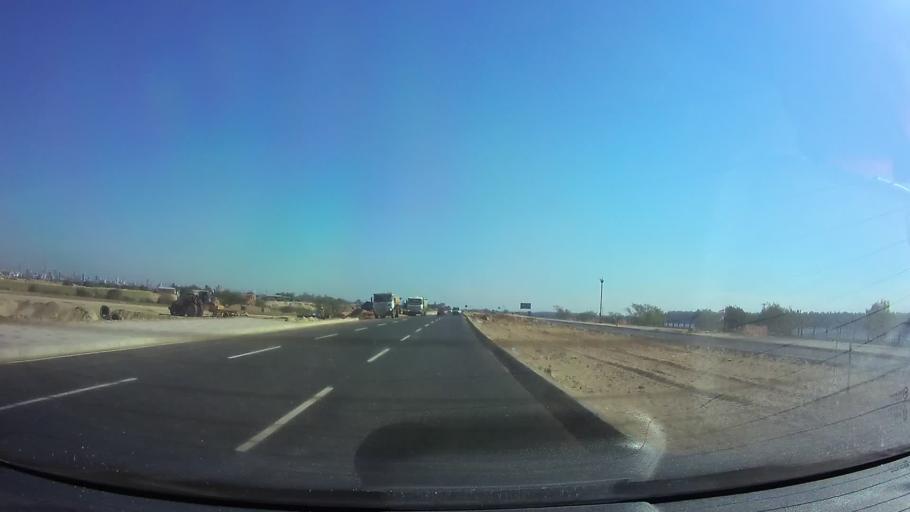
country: PY
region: Asuncion
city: Asuncion
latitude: -25.2461
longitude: -57.5943
